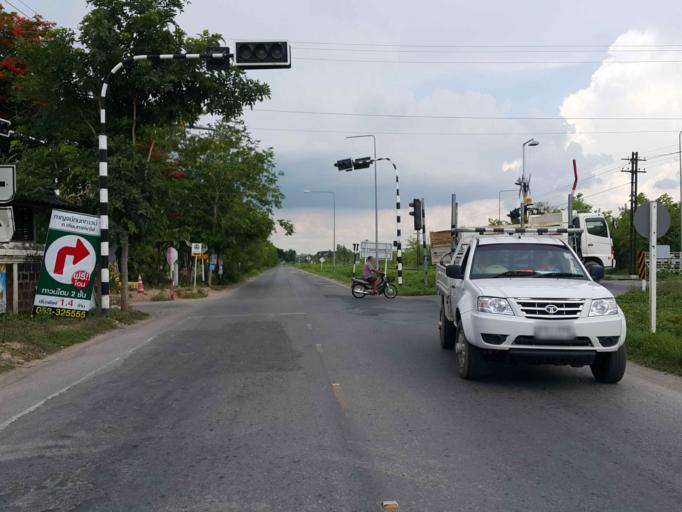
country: TH
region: Chiang Mai
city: Saraphi
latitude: 18.7473
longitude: 99.0260
